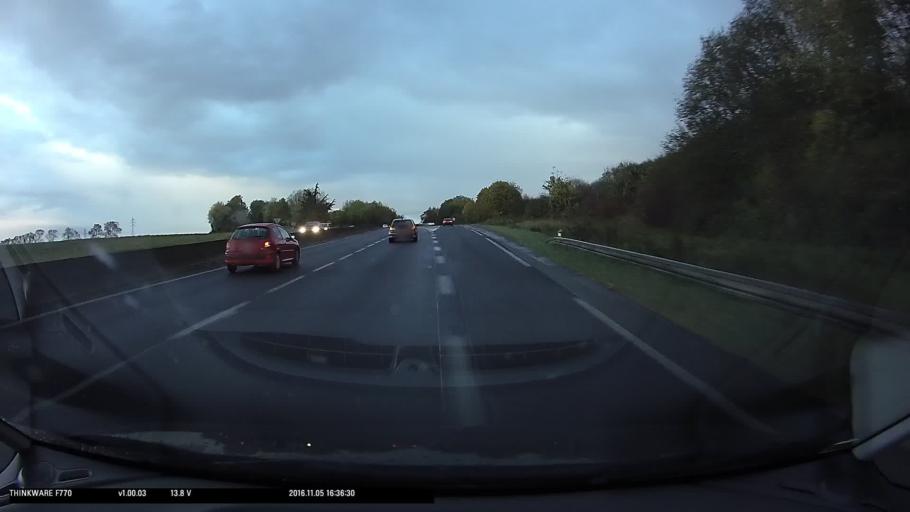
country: FR
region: Ile-de-France
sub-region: Departement du Val-d'Oise
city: Courdimanche
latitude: 49.0584
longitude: 2.0024
